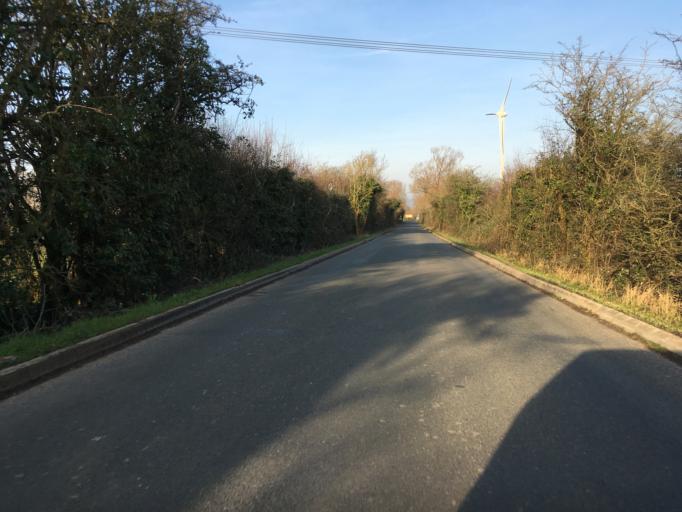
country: GB
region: Wales
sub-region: Newport
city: Bishton
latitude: 51.5672
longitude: -2.8691
